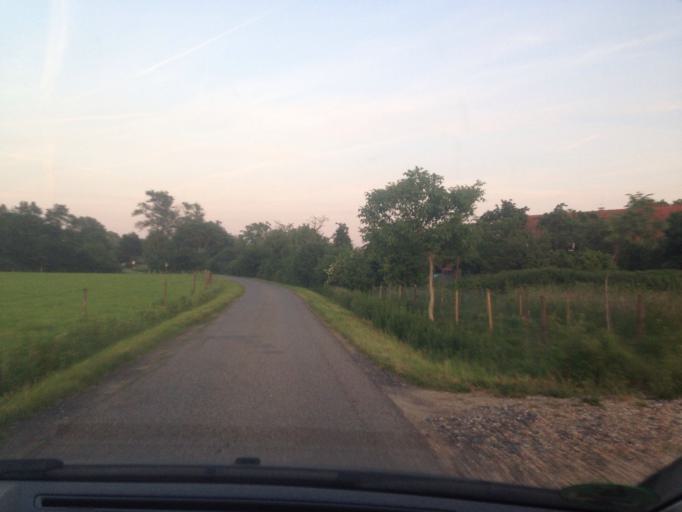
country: DE
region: North Rhine-Westphalia
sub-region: Regierungsbezirk Munster
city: Greven
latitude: 52.0178
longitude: 7.5566
